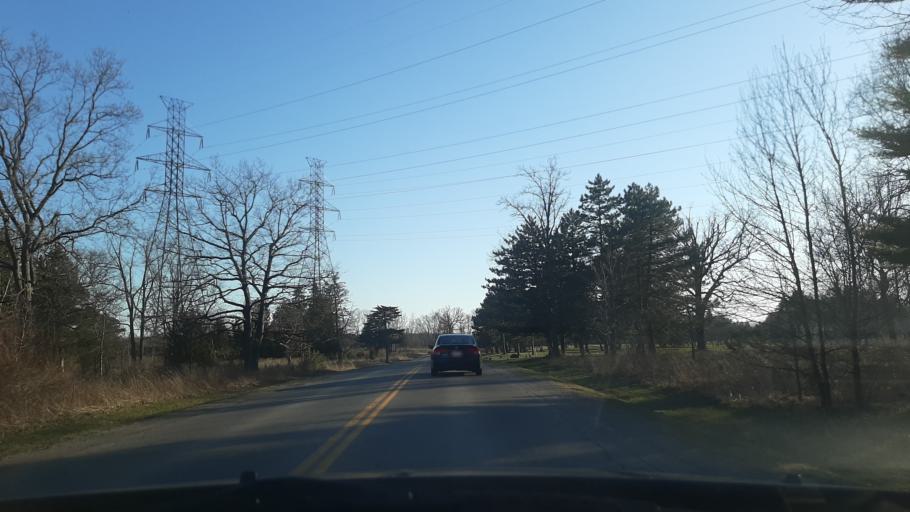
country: US
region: New York
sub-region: Niagara County
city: Lewiston
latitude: 43.1408
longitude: -79.0464
